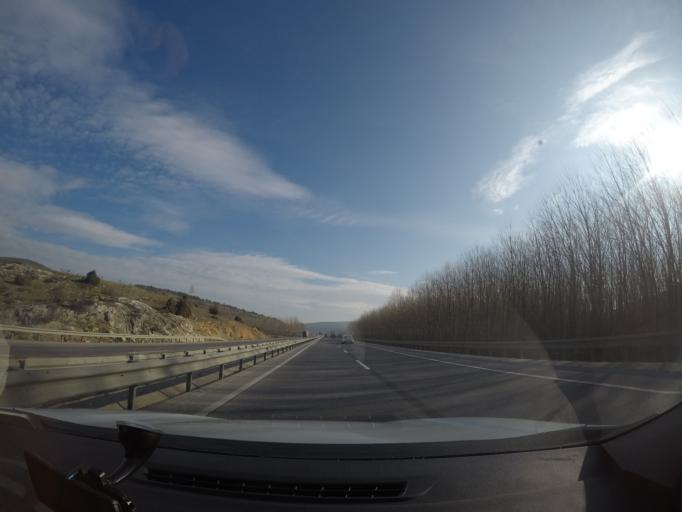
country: TR
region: Bilecik
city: Bozuyuk
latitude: 39.8952
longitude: 29.9786
